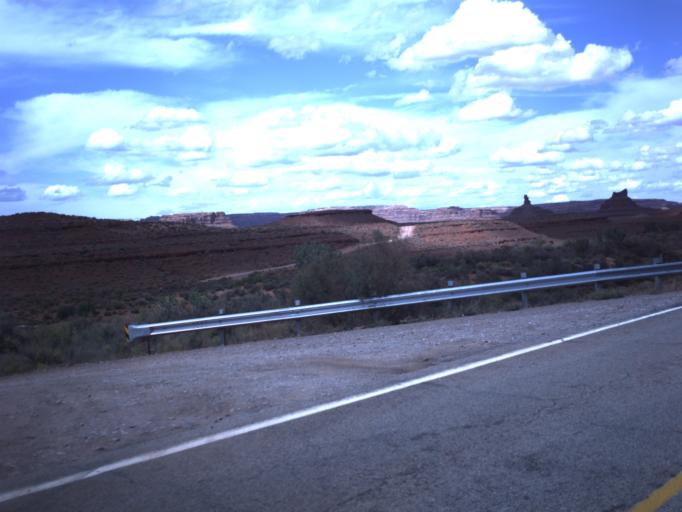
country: US
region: Utah
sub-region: San Juan County
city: Blanding
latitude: 37.2348
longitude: -109.8143
